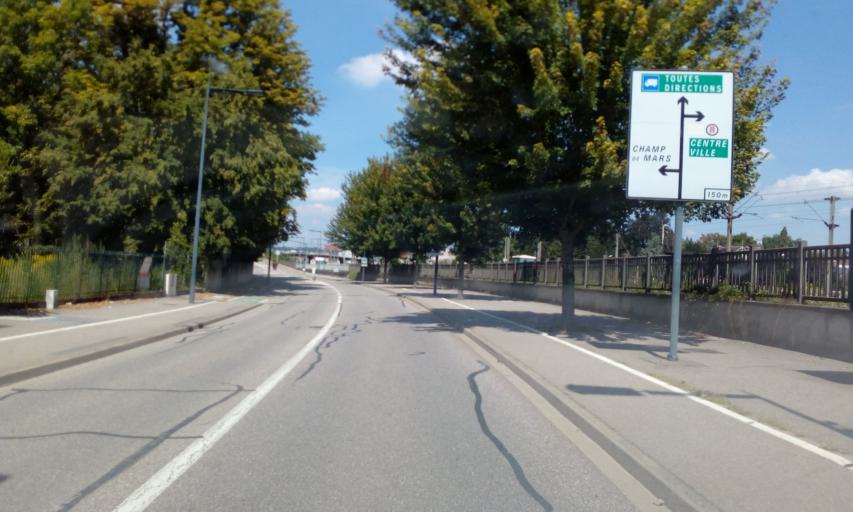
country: FR
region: Lorraine
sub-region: Departement de Meurthe-et-Moselle
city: Maidieres
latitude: 48.8973
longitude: 6.0520
